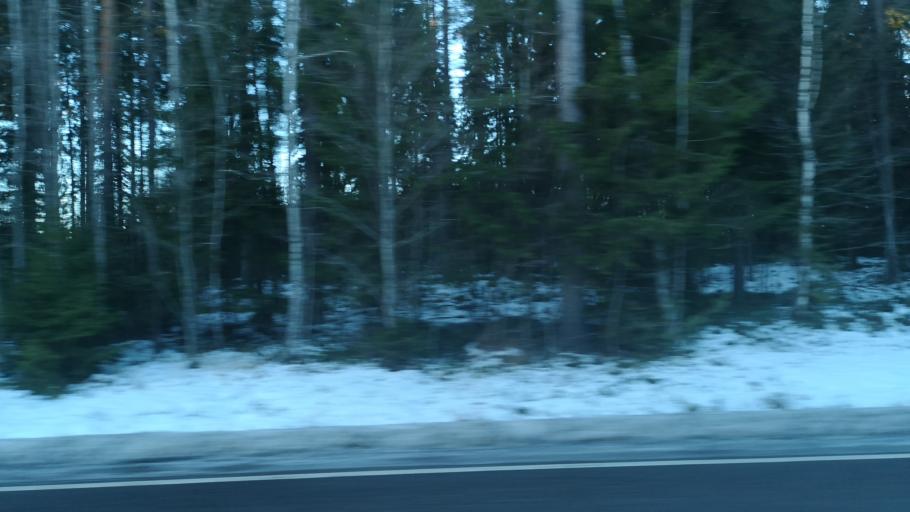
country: FI
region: Southern Savonia
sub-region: Pieksaemaeki
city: Juva
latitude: 61.9083
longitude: 28.0088
